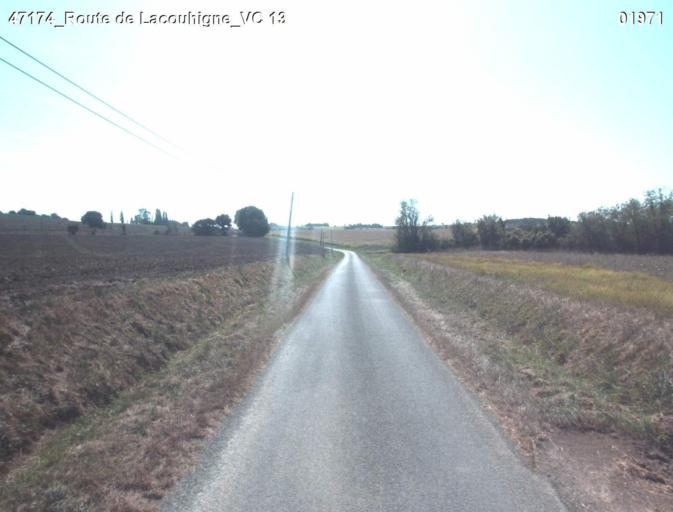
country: FR
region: Midi-Pyrenees
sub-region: Departement du Gers
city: Condom
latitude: 44.0285
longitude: 0.3735
